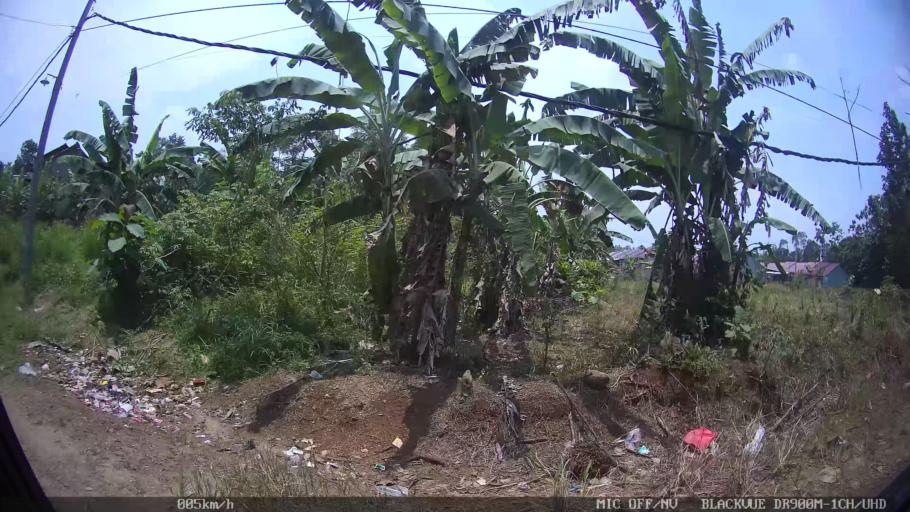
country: ID
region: Lampung
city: Natar
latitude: -5.3213
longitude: 105.2488
